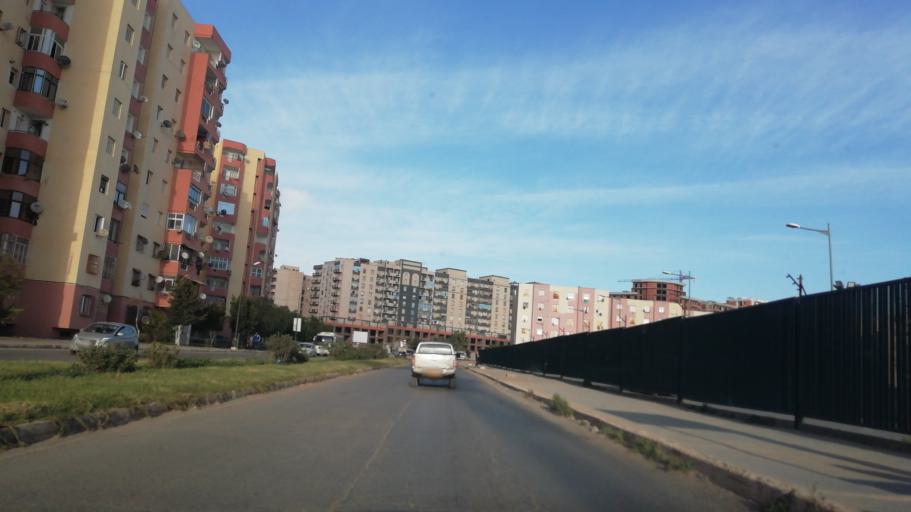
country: DZ
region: Oran
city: Bir el Djir
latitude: 35.7085
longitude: -0.5677
